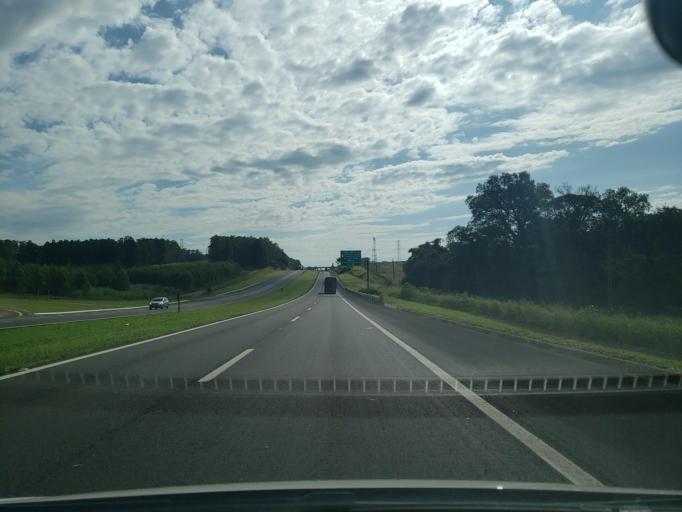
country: BR
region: Sao Paulo
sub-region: Lins
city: Lins
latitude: -21.6734
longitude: -49.7784
